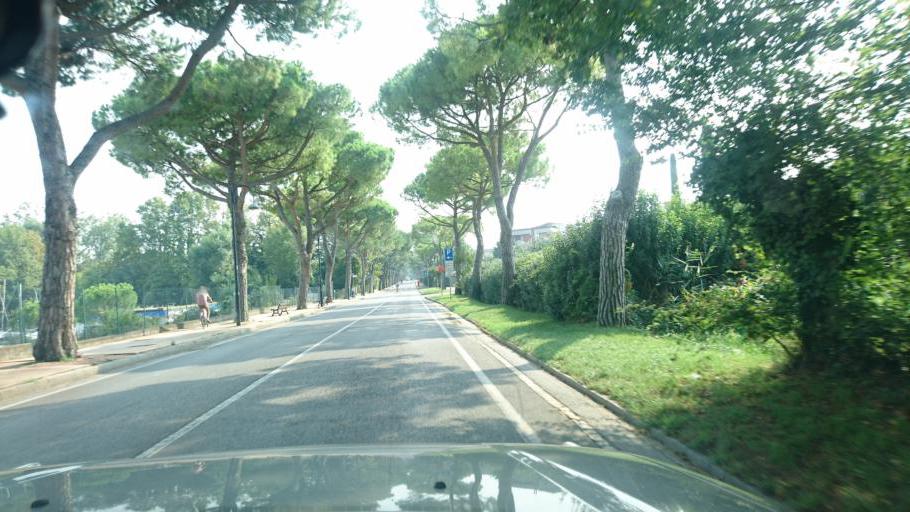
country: IT
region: Lombardy
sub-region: Provincia di Brescia
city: Desenzano del Garda
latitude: 45.4846
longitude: 10.5384
